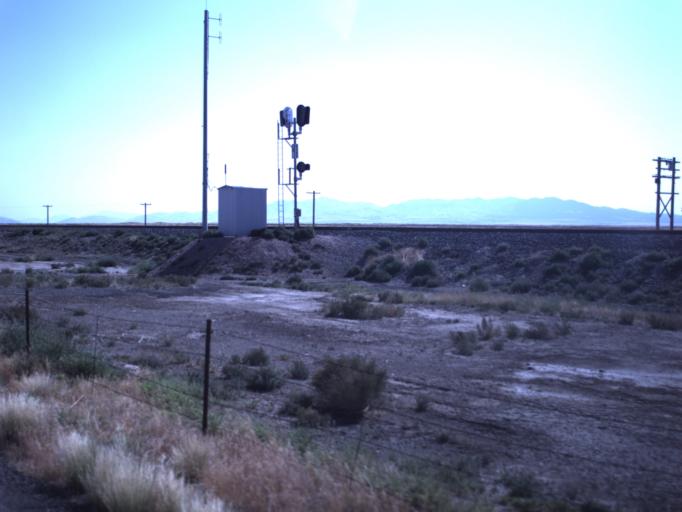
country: US
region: Utah
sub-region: Millard County
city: Delta
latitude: 39.1962
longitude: -112.6905
